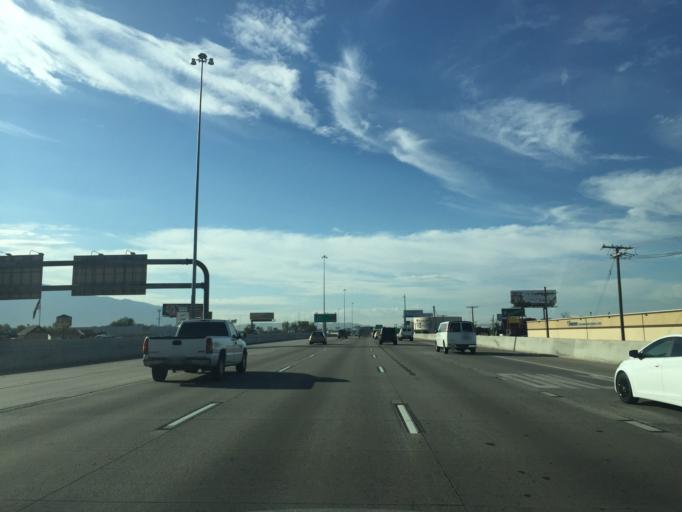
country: US
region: Utah
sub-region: Salt Lake County
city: South Salt Lake
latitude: 40.7096
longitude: -111.9042
